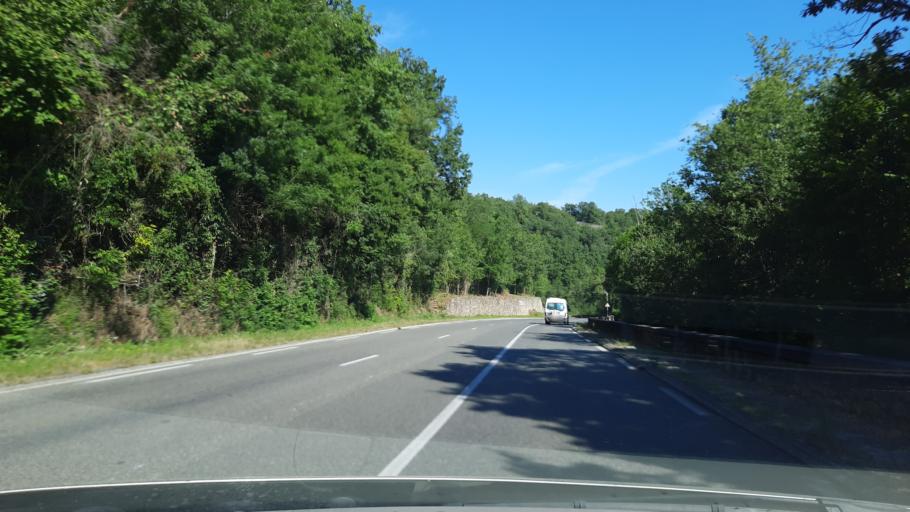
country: FR
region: Midi-Pyrenees
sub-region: Departement du Tarn-et-Garonne
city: Caylus
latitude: 44.2339
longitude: 1.7666
